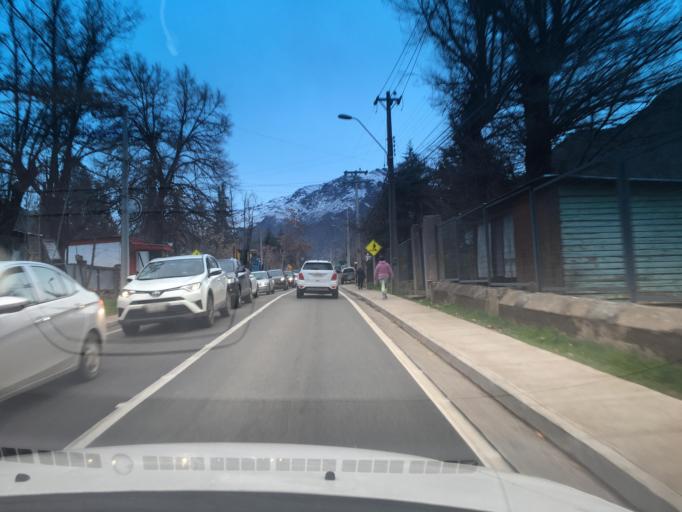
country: CL
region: Santiago Metropolitan
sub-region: Provincia de Cordillera
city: Puente Alto
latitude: -33.6899
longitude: -70.3357
